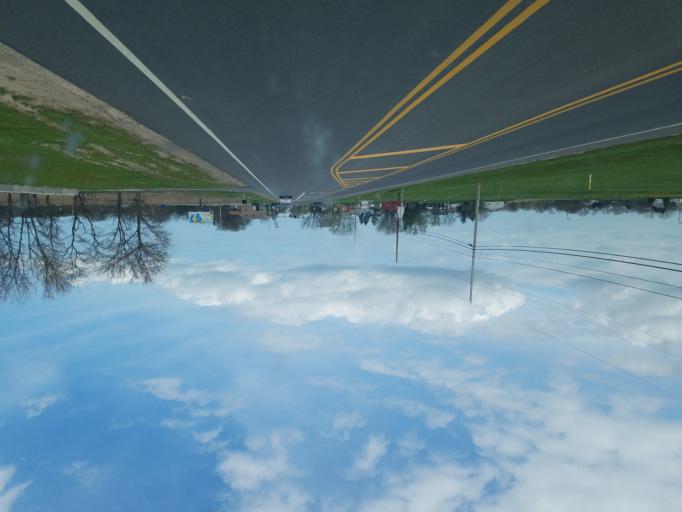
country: US
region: Ohio
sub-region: Erie County
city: Sandusky
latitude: 41.4073
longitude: -82.7272
